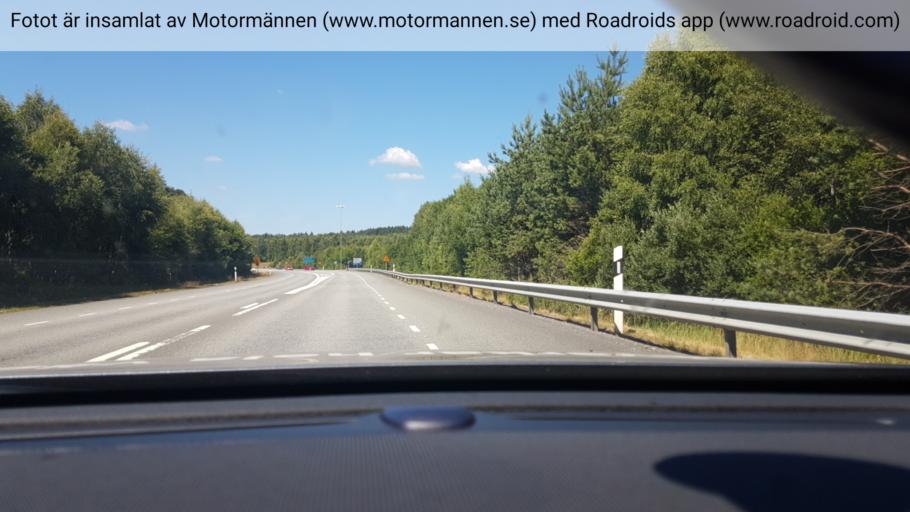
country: SE
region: Skane
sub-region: Hassleholms Kommun
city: Hassleholm
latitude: 56.1710
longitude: 13.8239
